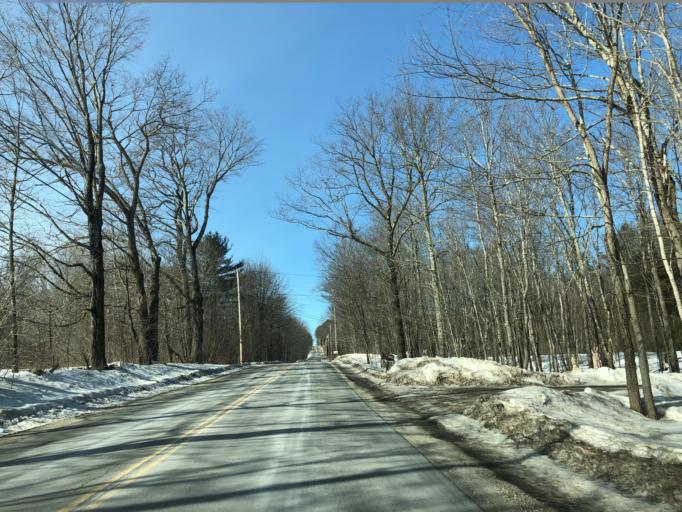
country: US
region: Maine
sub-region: Androscoggin County
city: Minot
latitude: 44.1496
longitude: -70.3343
